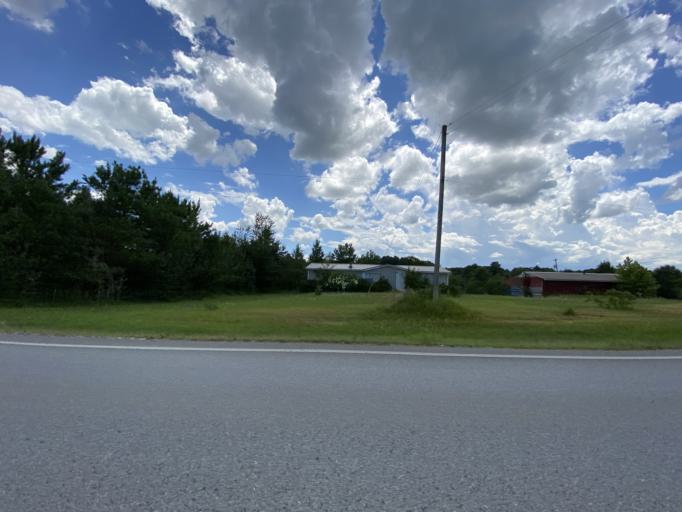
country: US
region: Alabama
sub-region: Lauderdale County
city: Underwood-Petersville
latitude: 34.9357
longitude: -87.8513
